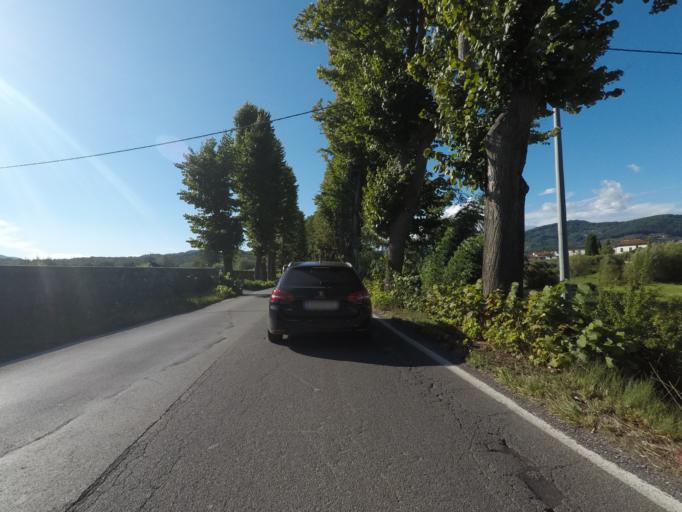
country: IT
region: Tuscany
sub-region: Provincia di Lucca
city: Lucca
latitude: 43.8726
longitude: 10.4960
